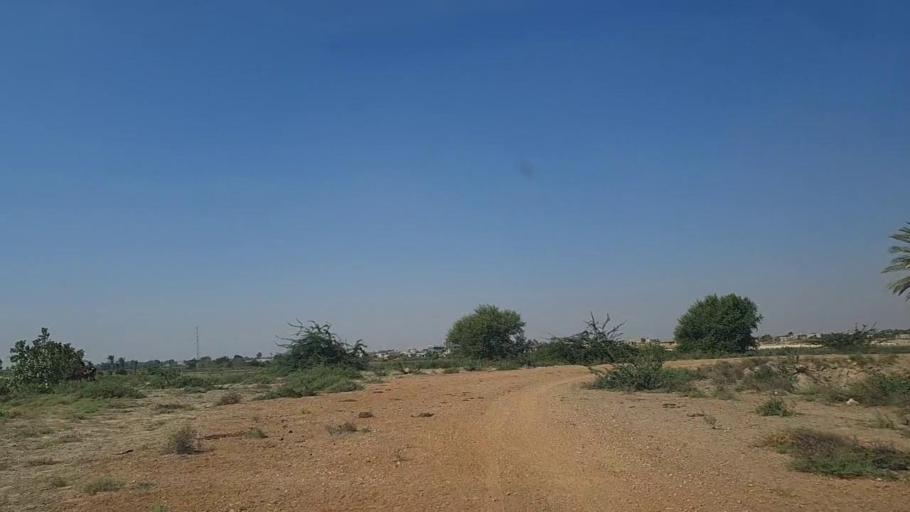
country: PK
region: Sindh
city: Thatta
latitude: 24.8103
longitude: 67.9864
